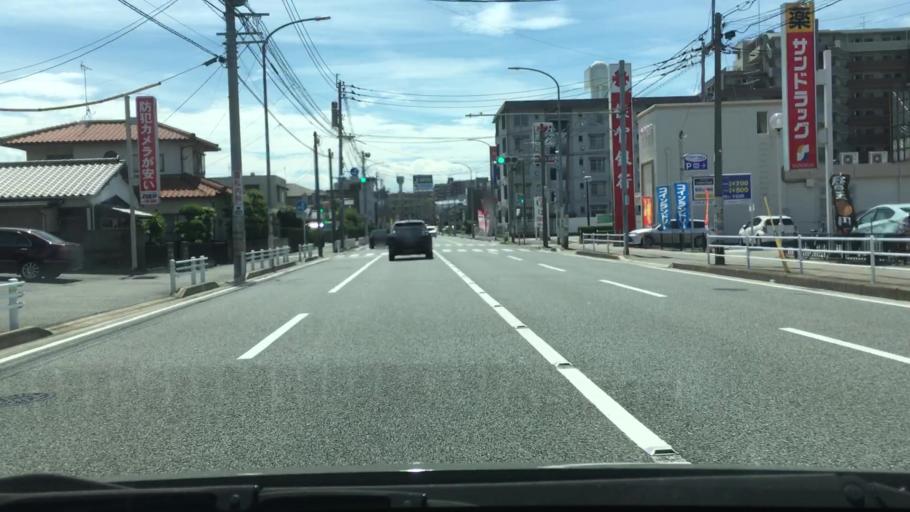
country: JP
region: Fukuoka
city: Onojo
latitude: 33.5513
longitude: 130.4578
